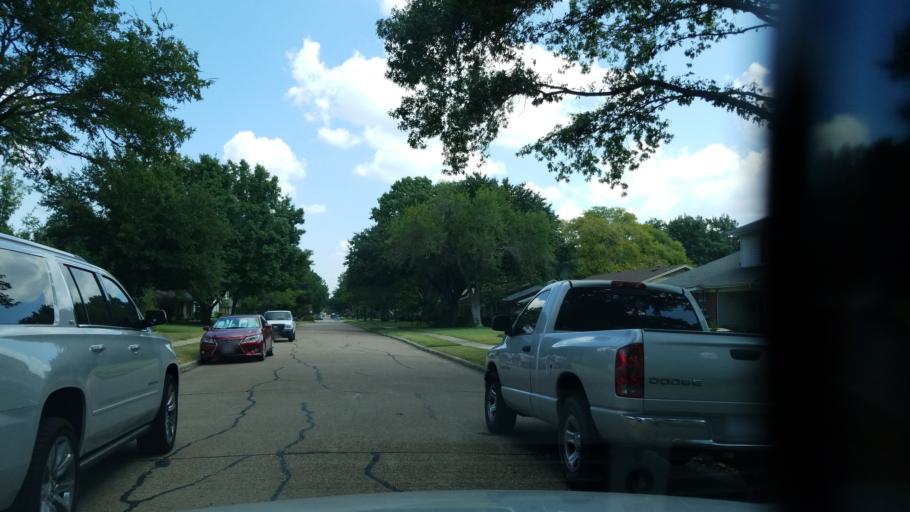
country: US
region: Texas
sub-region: Dallas County
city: Richardson
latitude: 32.9690
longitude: -96.7657
